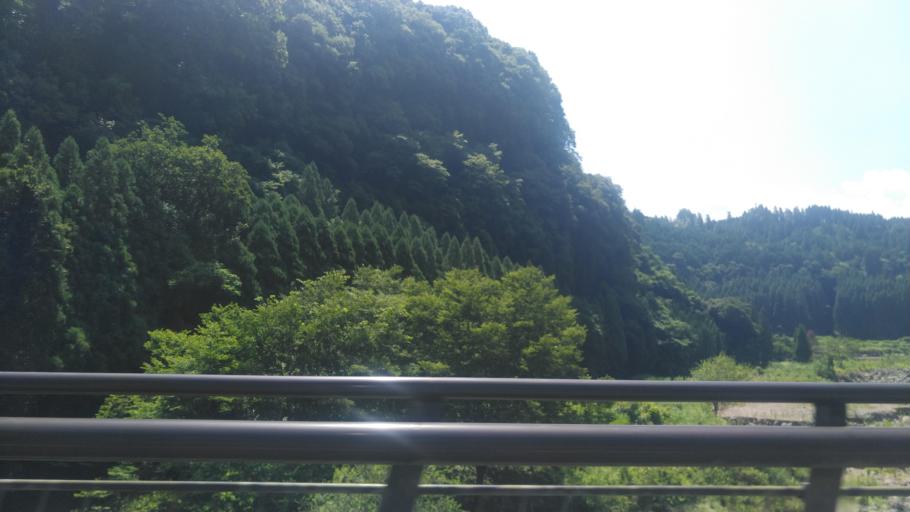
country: JP
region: Oita
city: Hita
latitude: 33.2625
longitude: 131.0108
